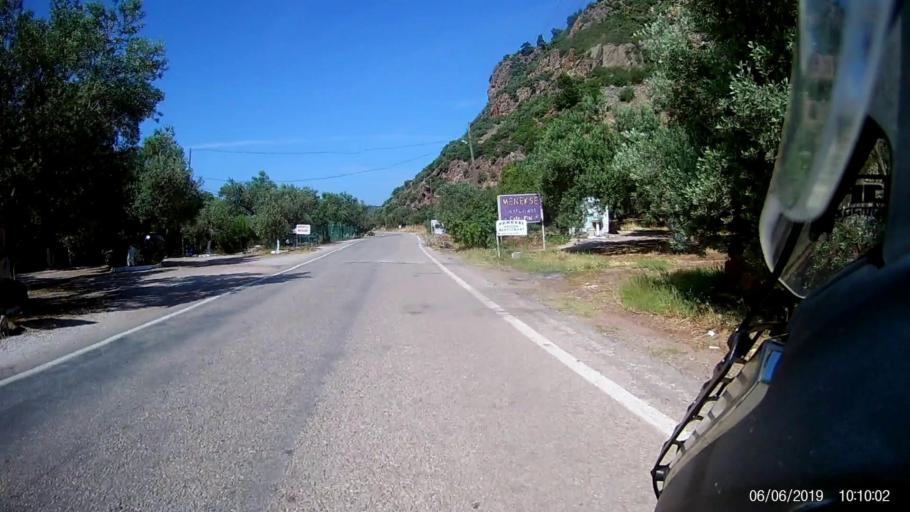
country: TR
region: Canakkale
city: Ayvacik
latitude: 39.5181
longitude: 26.4445
